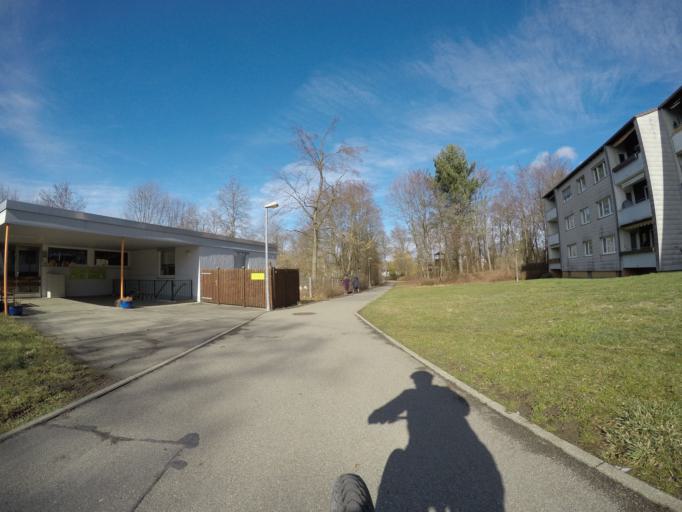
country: DE
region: Baden-Wuerttemberg
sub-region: Tuebingen Region
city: Reutlingen
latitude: 48.5190
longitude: 9.2123
